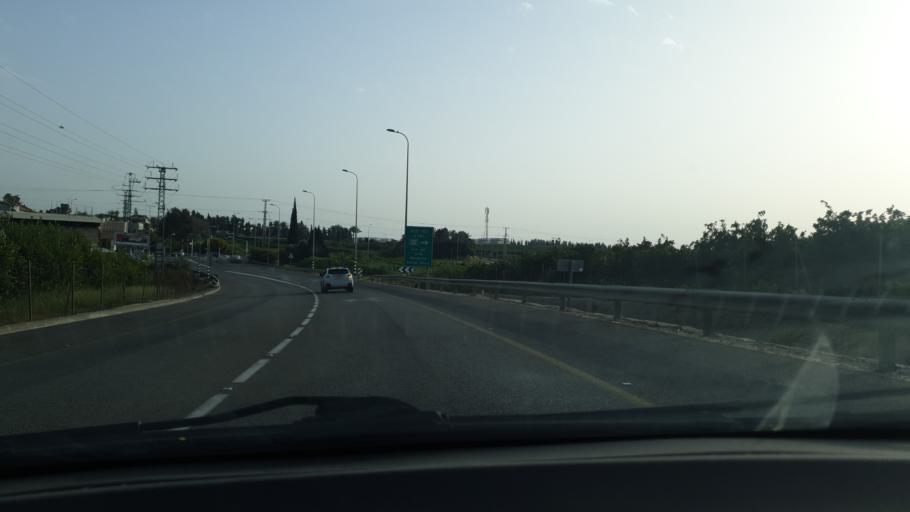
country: IL
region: Central District
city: Tel Mond
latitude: 32.2633
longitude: 34.9160
